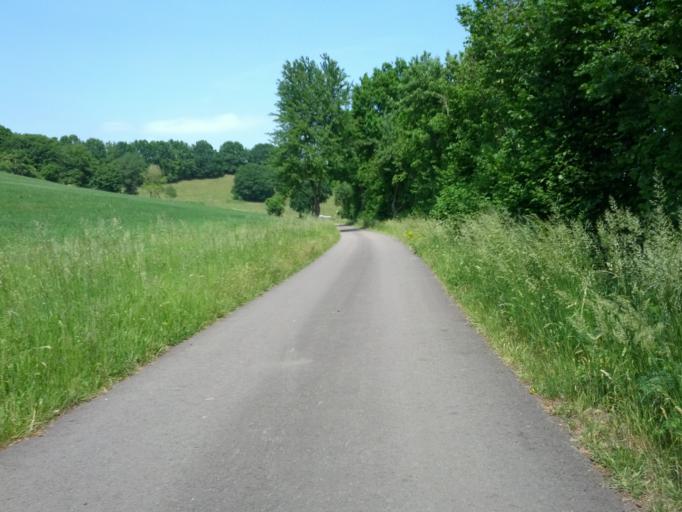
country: DE
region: Thuringia
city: Wiesenthal
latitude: 50.7200
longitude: 10.1635
